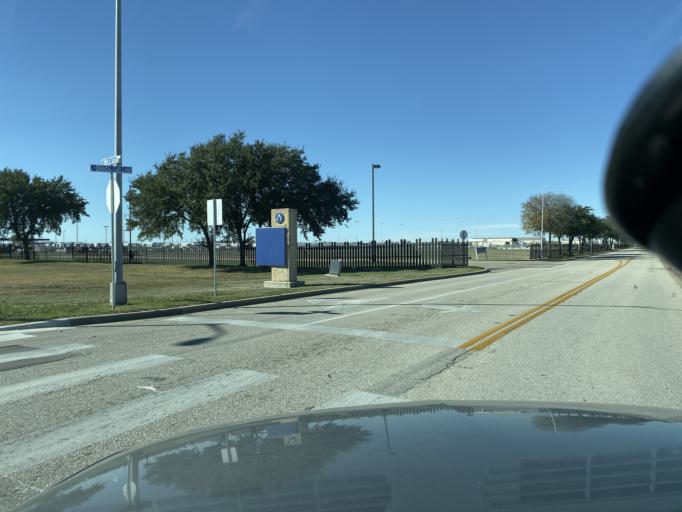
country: US
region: Texas
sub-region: Travis County
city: Hornsby Bend
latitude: 30.2104
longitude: -97.6689
